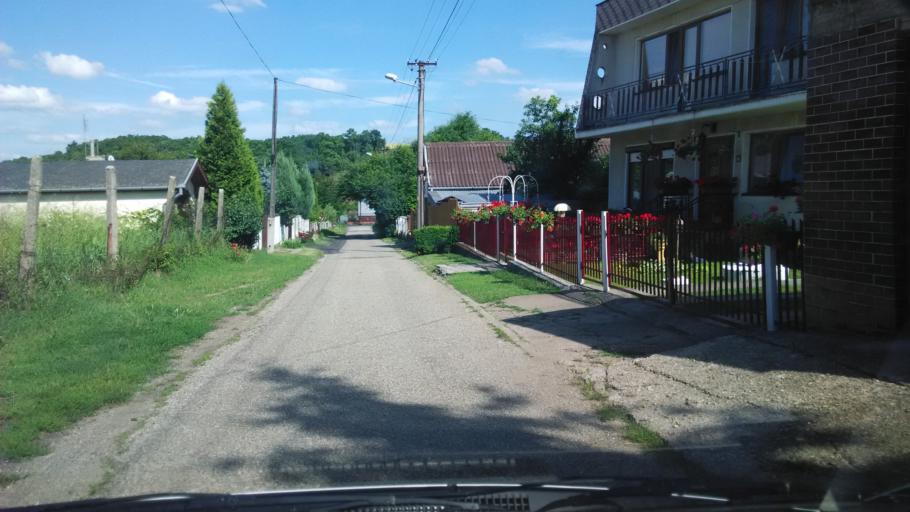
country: SK
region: Nitriansky
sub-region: Okres Nitra
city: Vrable
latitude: 48.1139
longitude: 18.3896
